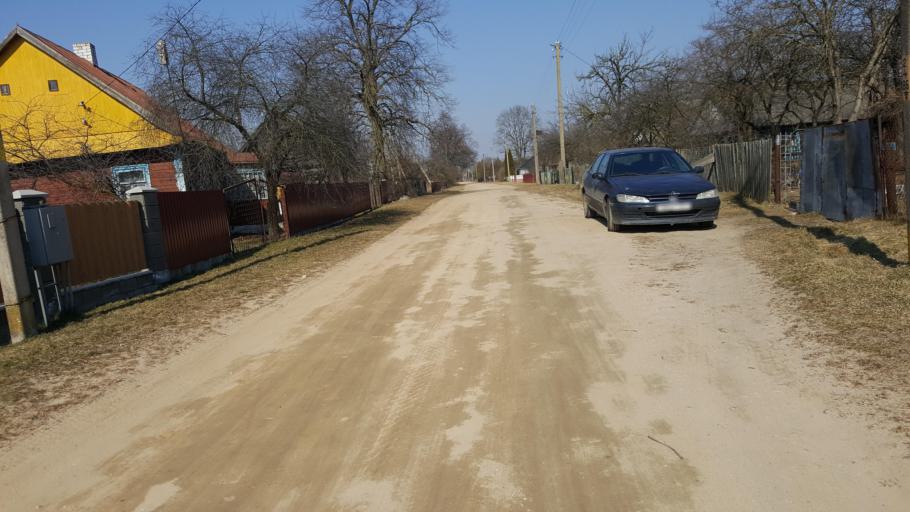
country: BY
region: Brest
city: Kamyanyets
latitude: 52.3113
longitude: 23.9193
